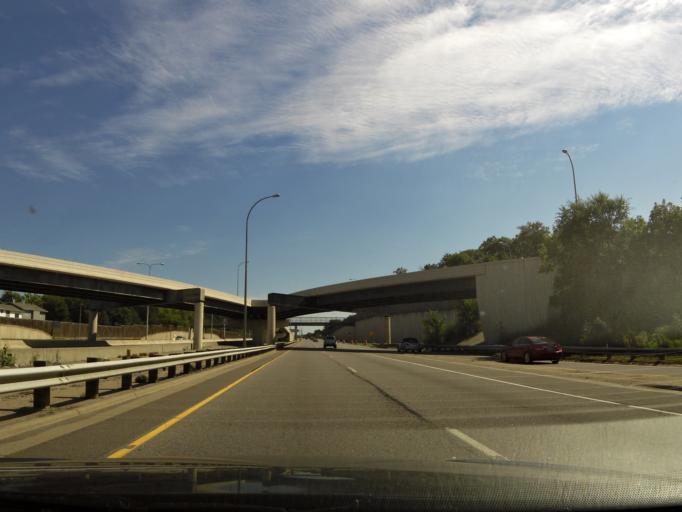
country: US
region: Minnesota
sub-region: Hennepin County
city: Saint Louis Park
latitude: 44.9705
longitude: -93.3386
